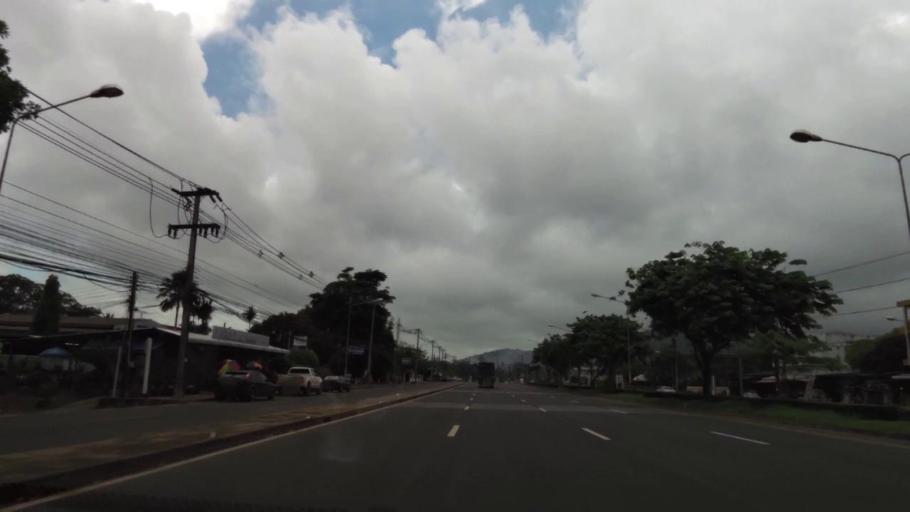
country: TH
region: Chanthaburi
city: Khlung
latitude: 12.4641
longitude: 102.2234
